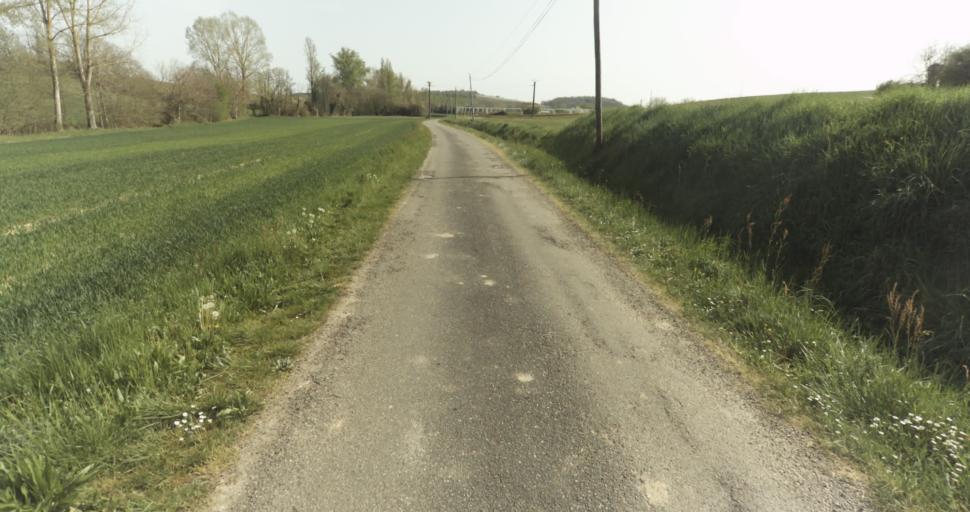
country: FR
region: Midi-Pyrenees
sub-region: Departement du Tarn-et-Garonne
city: Moissac
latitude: 44.1367
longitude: 1.1600
